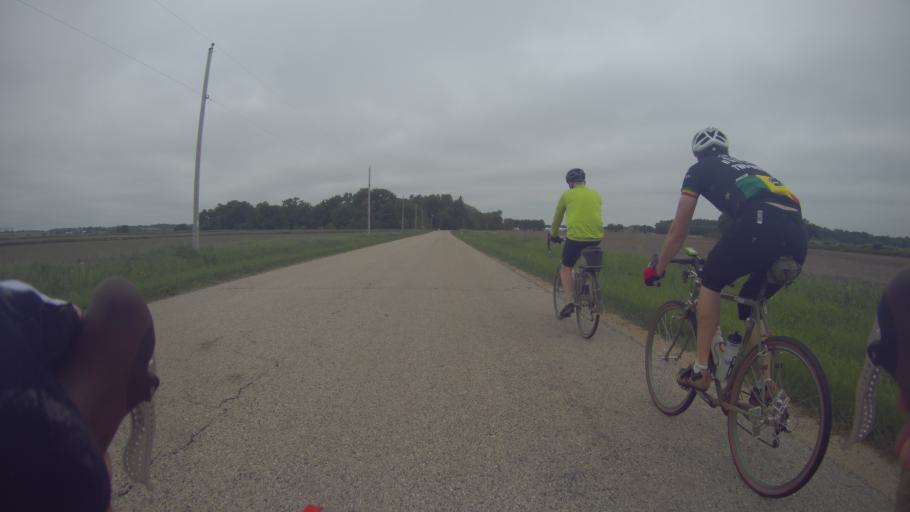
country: US
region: Wisconsin
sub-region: Green County
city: Brooklyn
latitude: 42.8719
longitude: -89.3945
